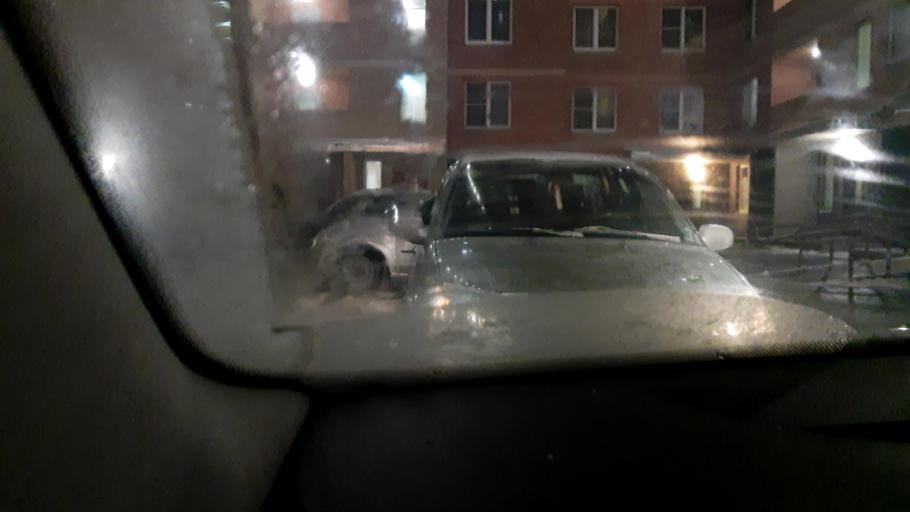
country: RU
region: Moskovskaya
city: Zheleznodorozhnyy
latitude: 55.7278
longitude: 37.9765
